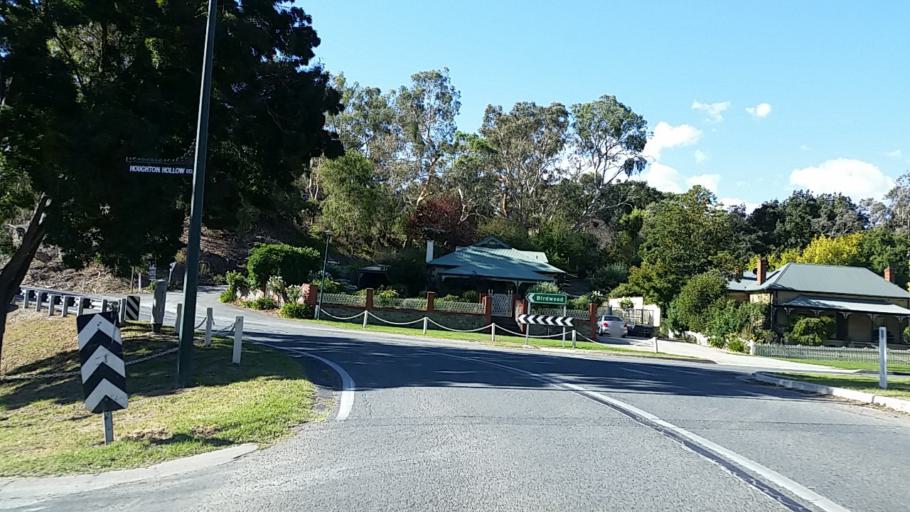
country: AU
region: South Australia
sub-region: Tea Tree Gully
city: Golden Grove
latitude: -34.8285
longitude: 138.7616
